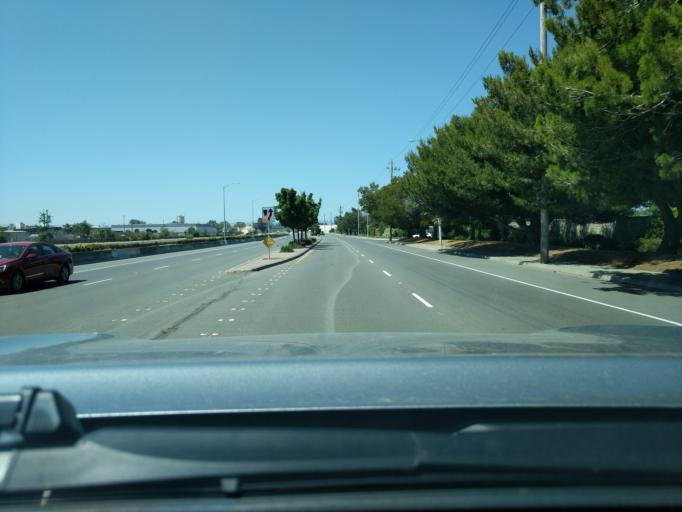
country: US
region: California
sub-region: Alameda County
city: Union City
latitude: 37.6168
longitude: -122.0630
